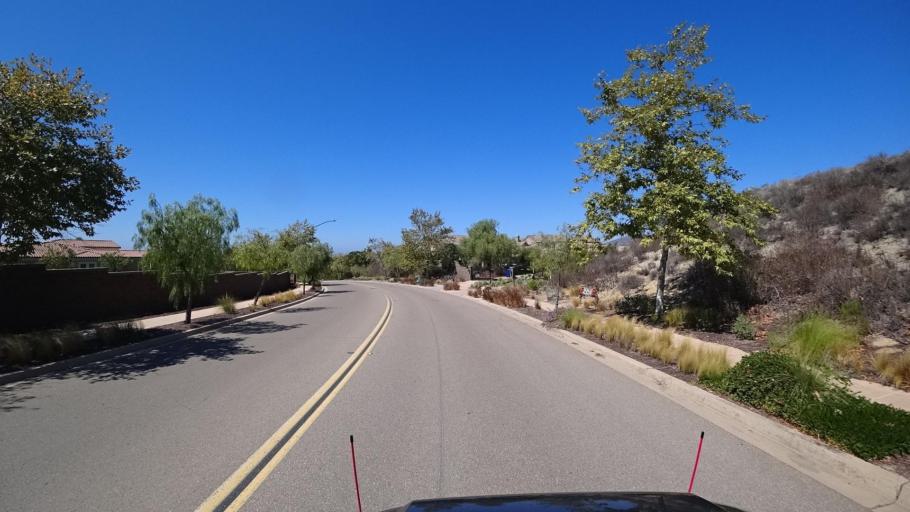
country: US
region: California
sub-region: San Diego County
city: Fairbanks Ranch
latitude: 33.0178
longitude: -117.1510
